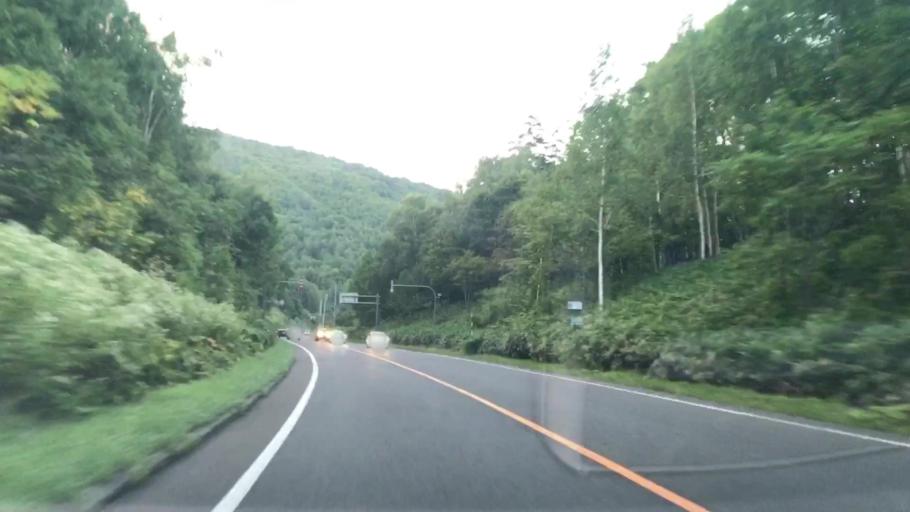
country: JP
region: Hokkaido
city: Sapporo
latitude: 42.9069
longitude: 141.1215
